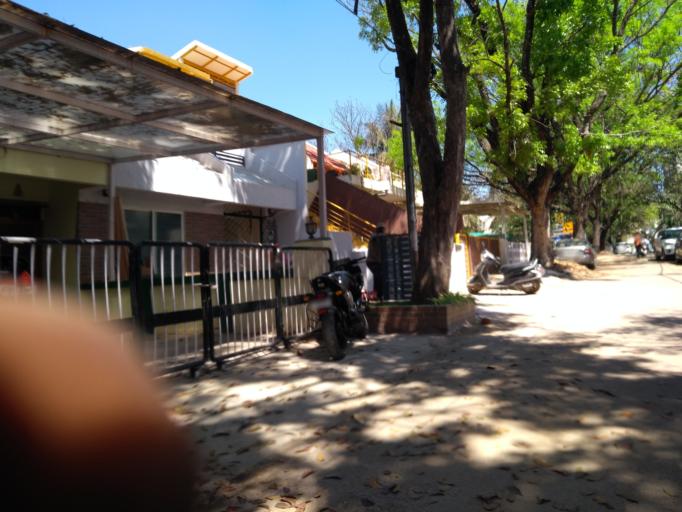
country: IN
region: Karnataka
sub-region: Bangalore Urban
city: Bangalore
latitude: 12.9683
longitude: 77.6533
